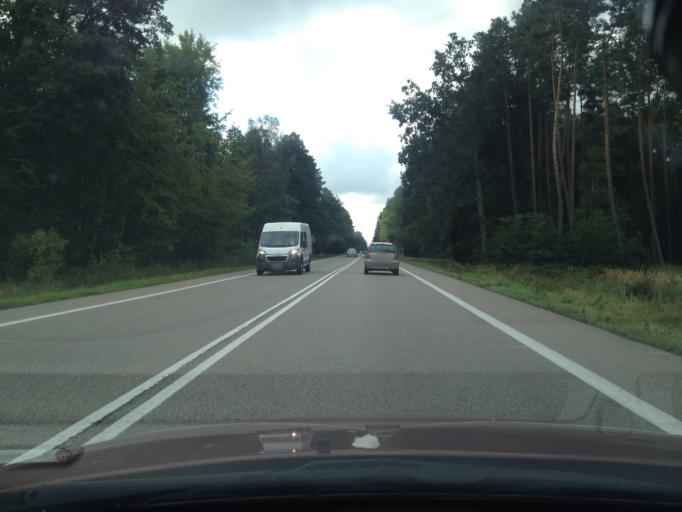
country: PL
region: West Pomeranian Voivodeship
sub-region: Powiat goleniowski
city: Goleniow
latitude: 53.6597
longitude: 14.8152
